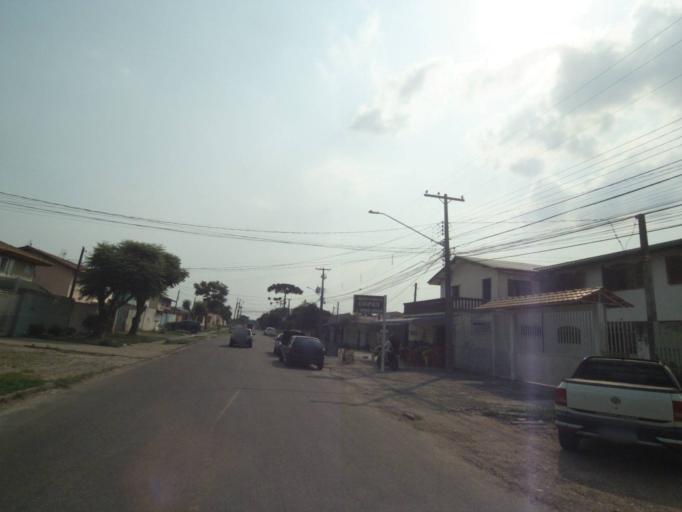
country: BR
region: Parana
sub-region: Sao Jose Dos Pinhais
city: Sao Jose dos Pinhais
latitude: -25.5261
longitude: -49.2284
